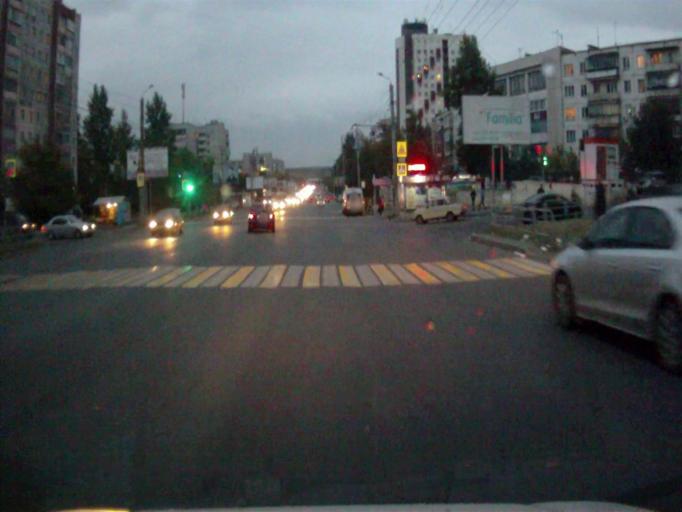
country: RU
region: Chelyabinsk
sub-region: Gorod Chelyabinsk
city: Chelyabinsk
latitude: 55.1844
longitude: 61.3326
